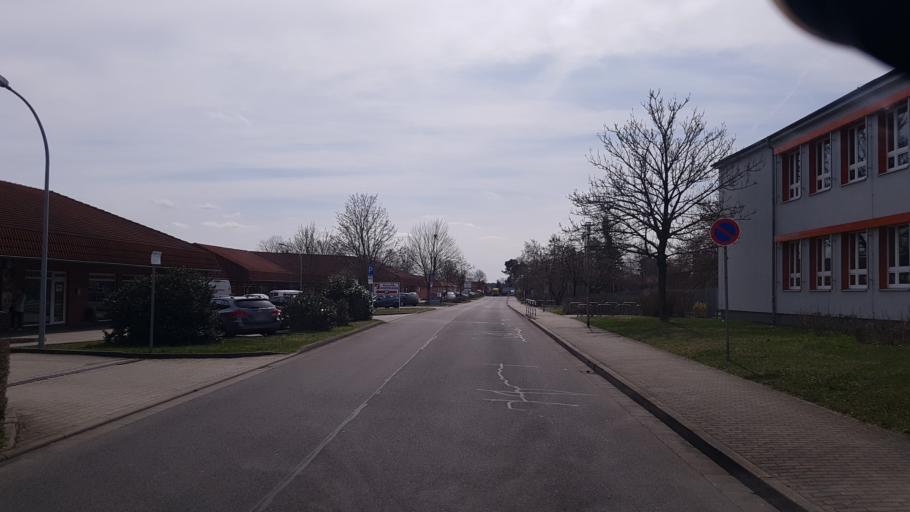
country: DE
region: Brandenburg
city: Schipkau
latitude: 51.5182
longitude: 13.8994
